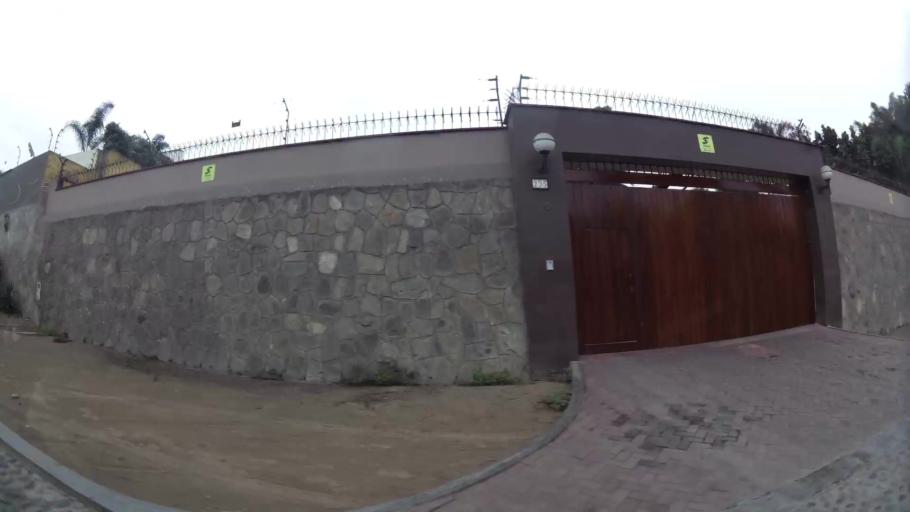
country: PE
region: Lima
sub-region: Lima
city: La Molina
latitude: -12.0775
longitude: -76.9318
